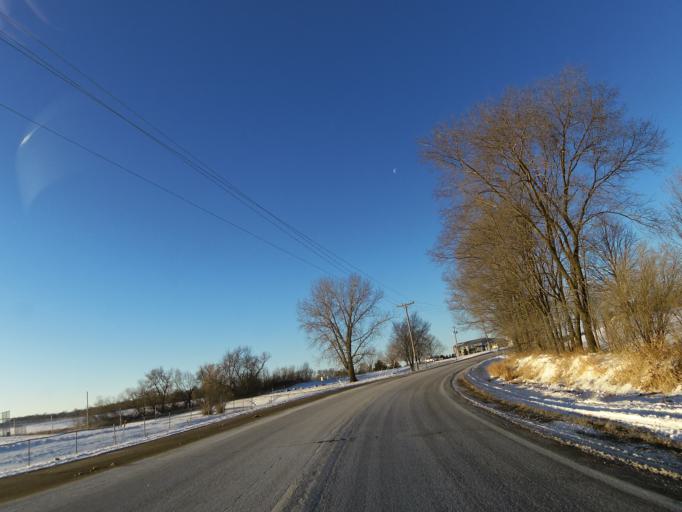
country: US
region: Minnesota
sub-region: Scott County
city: Prior Lake
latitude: 44.6529
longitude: -93.4688
